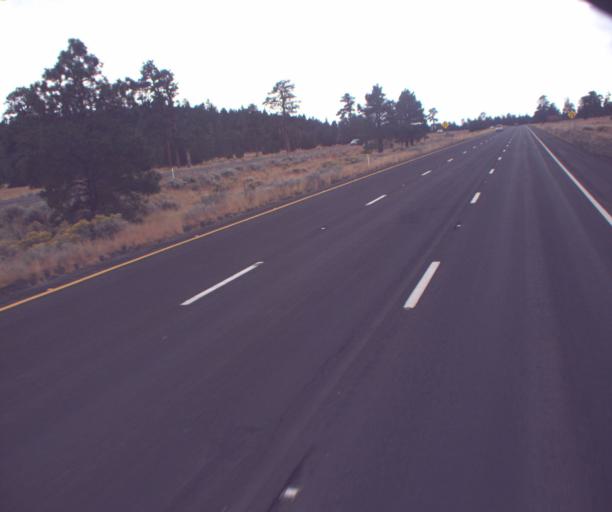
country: US
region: Arizona
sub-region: Coconino County
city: Flagstaff
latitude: 35.3876
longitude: -111.5796
